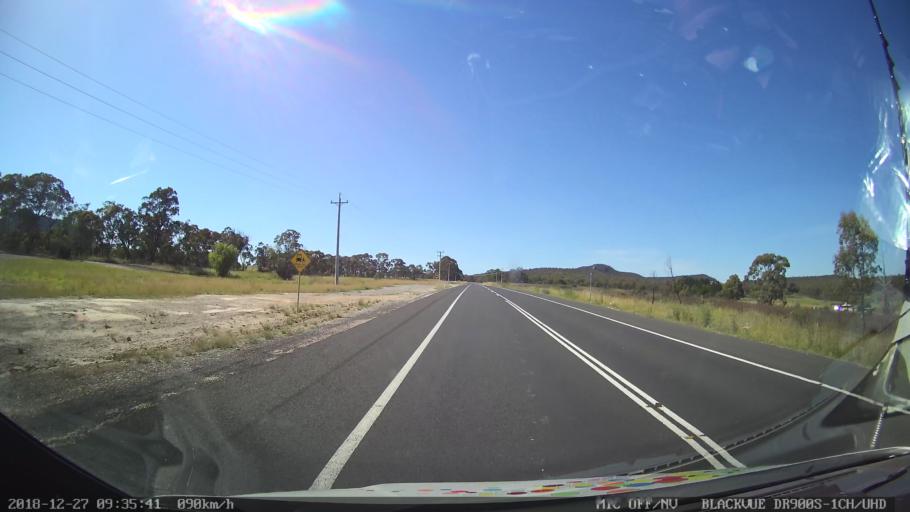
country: AU
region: New South Wales
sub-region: Lithgow
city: Portland
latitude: -33.2419
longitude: 150.0319
